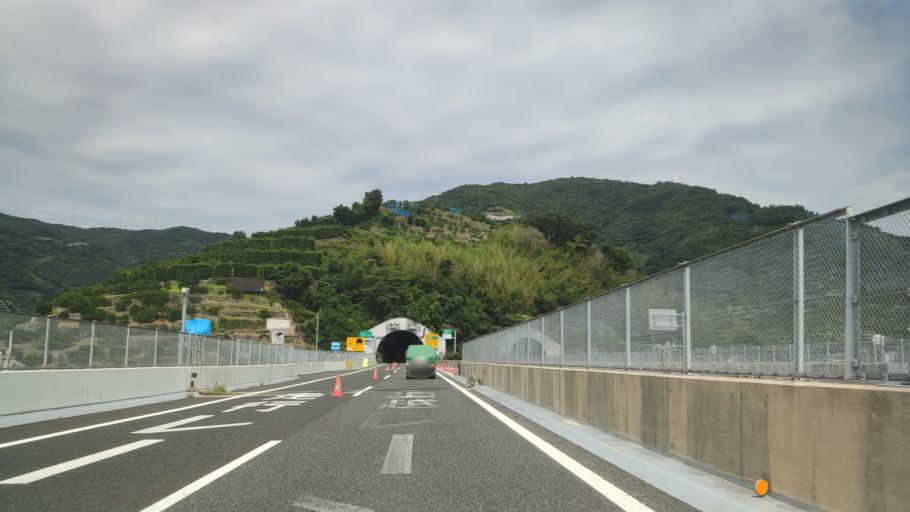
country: JP
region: Wakayama
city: Kainan
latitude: 34.0757
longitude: 135.2008
